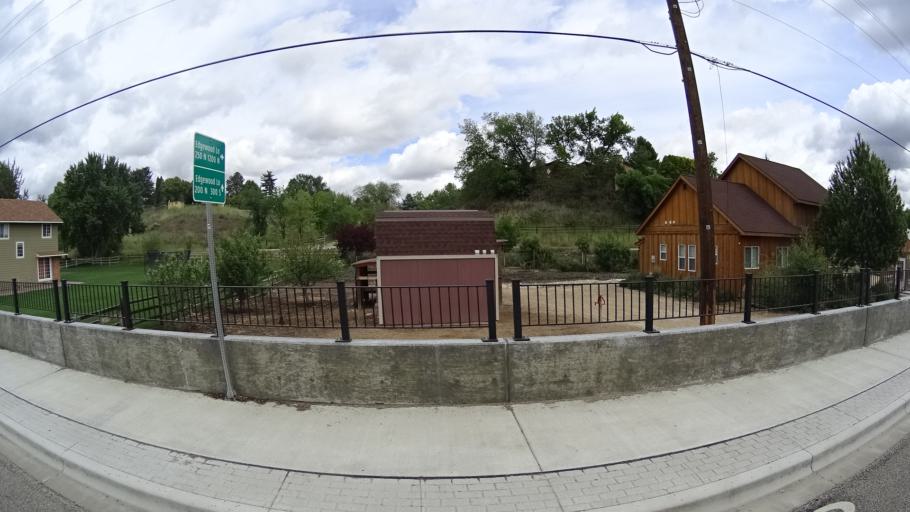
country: US
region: Idaho
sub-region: Ada County
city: Eagle
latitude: 43.6957
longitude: -116.3289
